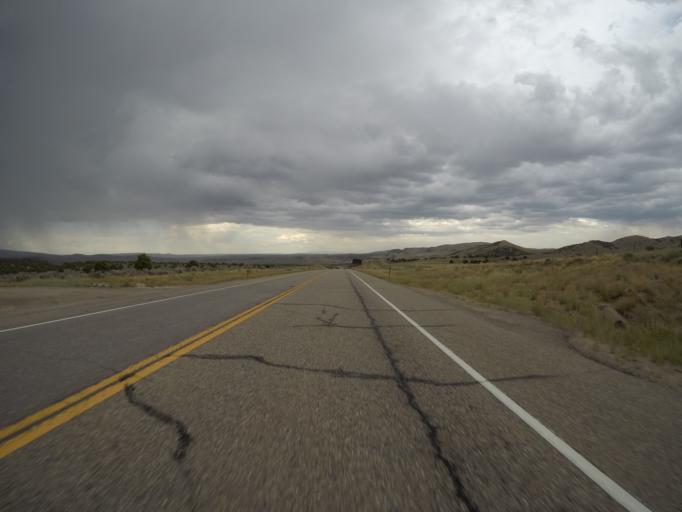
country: US
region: Colorado
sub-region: Rio Blanco County
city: Rangely
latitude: 40.3751
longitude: -108.3753
